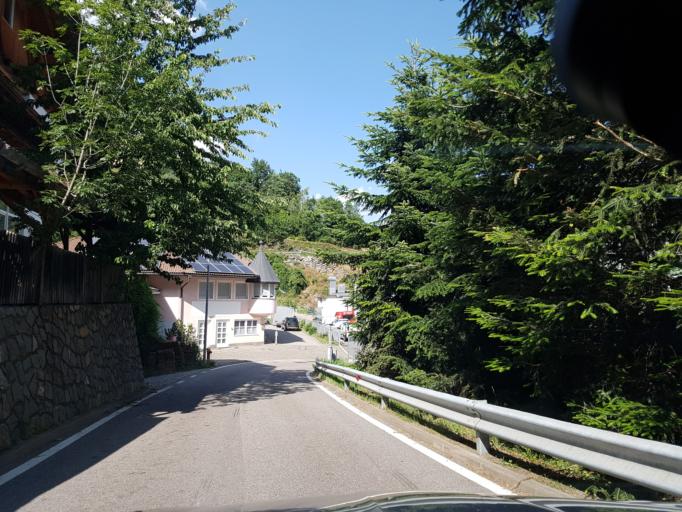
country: IT
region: Trentino-Alto Adige
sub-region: Bolzano
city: Villandro - Villanders
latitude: 46.6164
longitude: 11.5334
